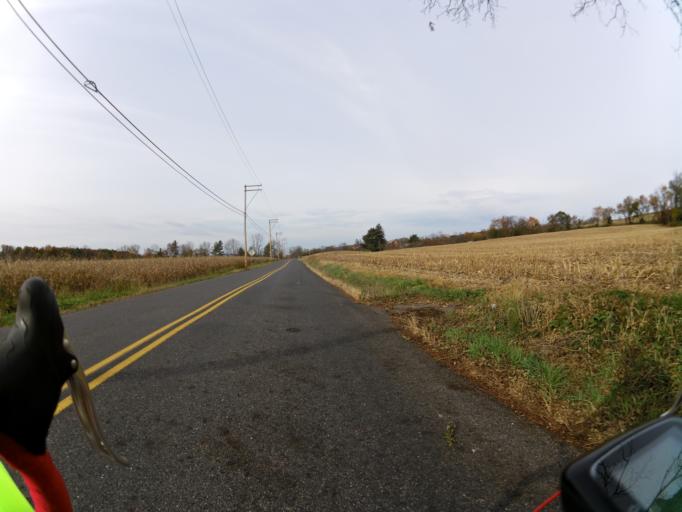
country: US
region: Pennsylvania
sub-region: Union County
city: New Columbia
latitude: 41.0534
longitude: -76.9078
